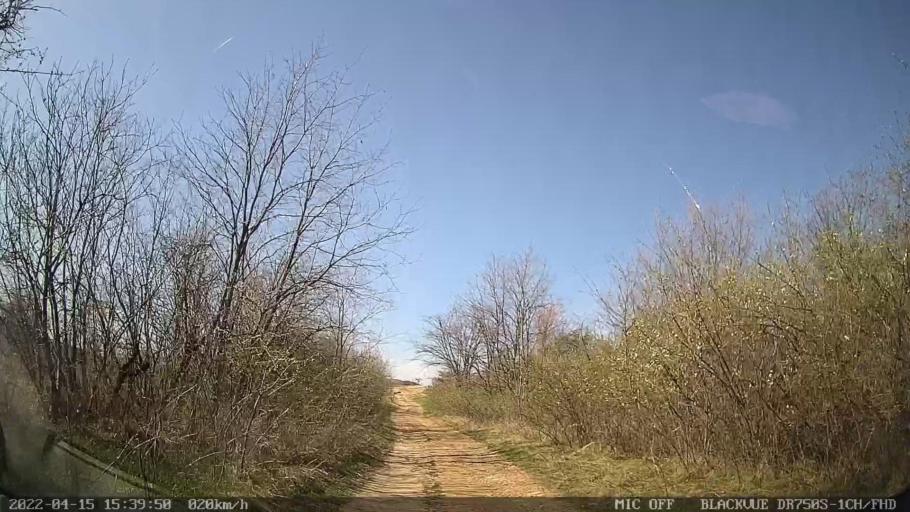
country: MD
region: Raionul Ocnita
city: Otaci
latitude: 48.3543
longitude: 27.9266
